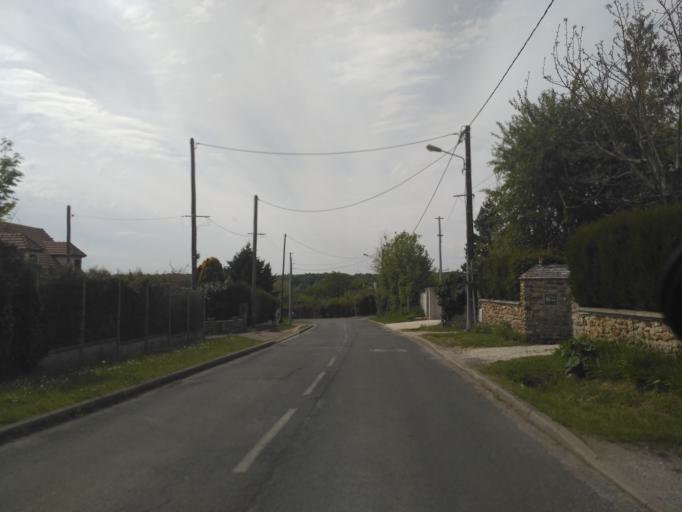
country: FR
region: Ile-de-France
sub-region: Departement de Seine-et-Marne
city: Chaumes-en-Brie
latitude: 48.6657
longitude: 2.8314
